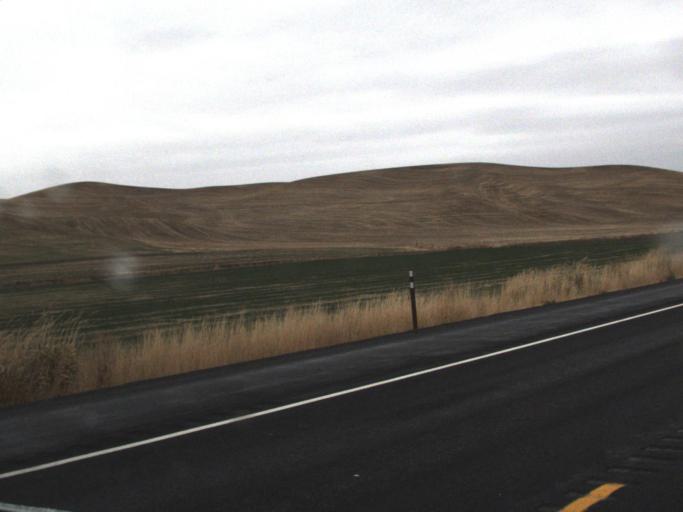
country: US
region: Washington
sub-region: Whitman County
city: Colfax
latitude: 46.8008
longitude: -117.3159
